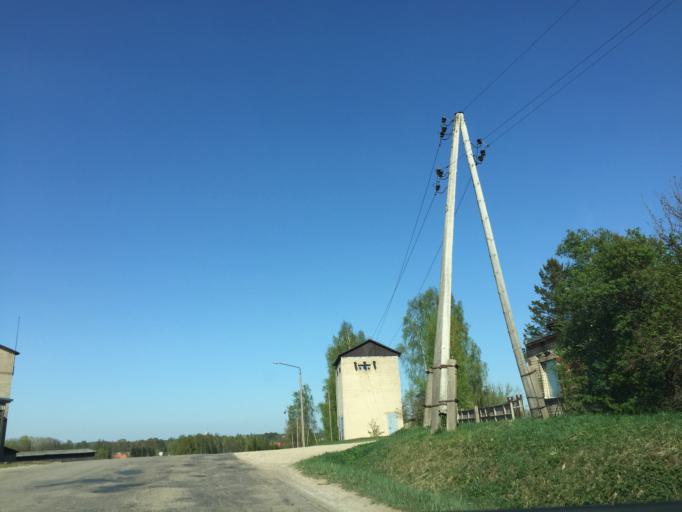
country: LV
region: Skriveri
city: Skriveri
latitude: 56.8422
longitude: 25.1456
